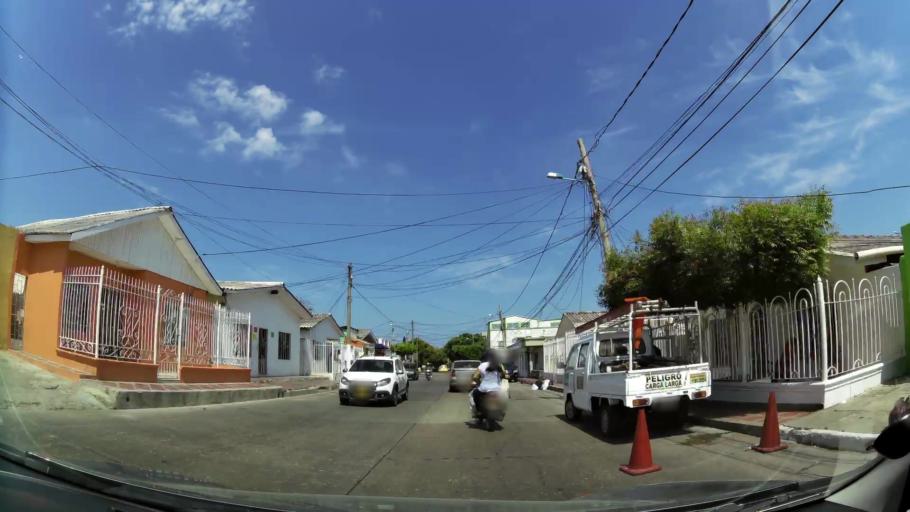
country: CO
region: Atlantico
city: Barranquilla
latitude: 10.9629
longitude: -74.8029
